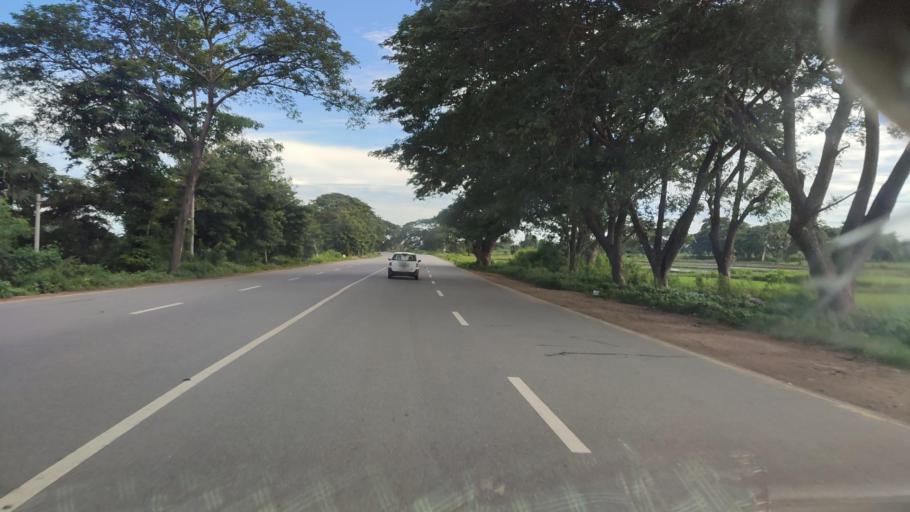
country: MM
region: Mandalay
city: Yamethin
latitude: 20.2290
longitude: 96.1795
